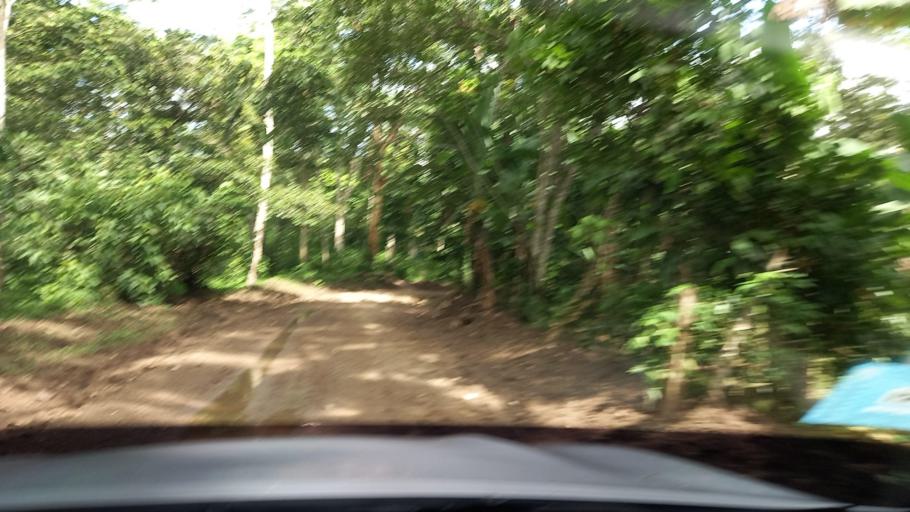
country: NI
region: Jinotega
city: San Jose de Bocay
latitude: 13.4152
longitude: -85.7045
